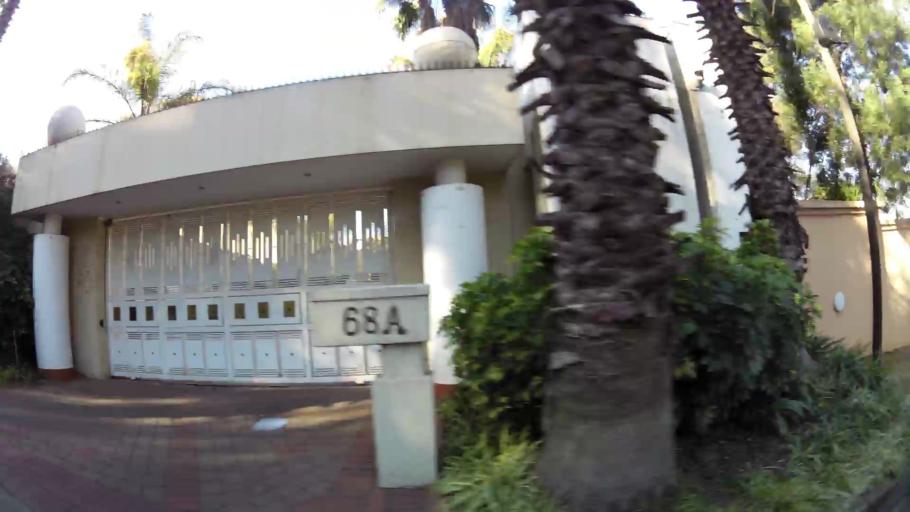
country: ZA
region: Gauteng
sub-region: City of Johannesburg Metropolitan Municipality
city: Johannesburg
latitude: -26.1163
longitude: 28.0661
